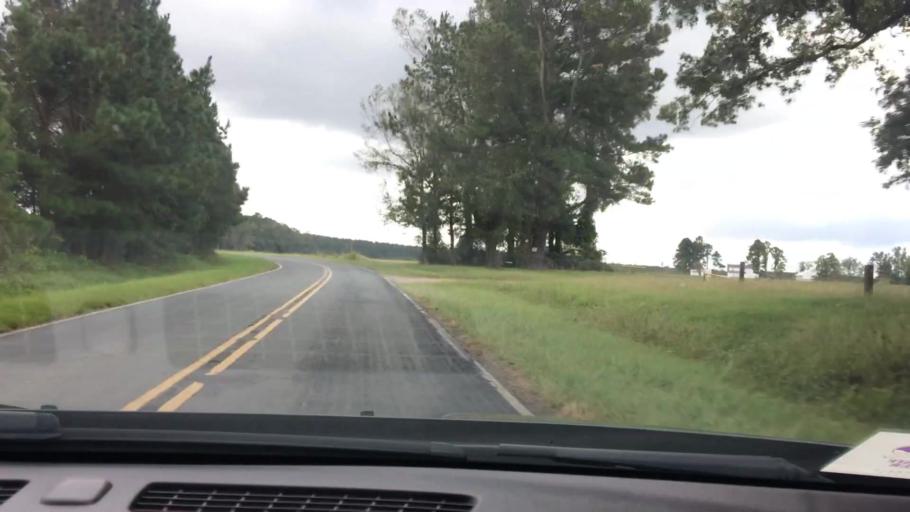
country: US
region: North Carolina
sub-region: Greene County
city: Maury
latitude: 35.5240
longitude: -77.5426
